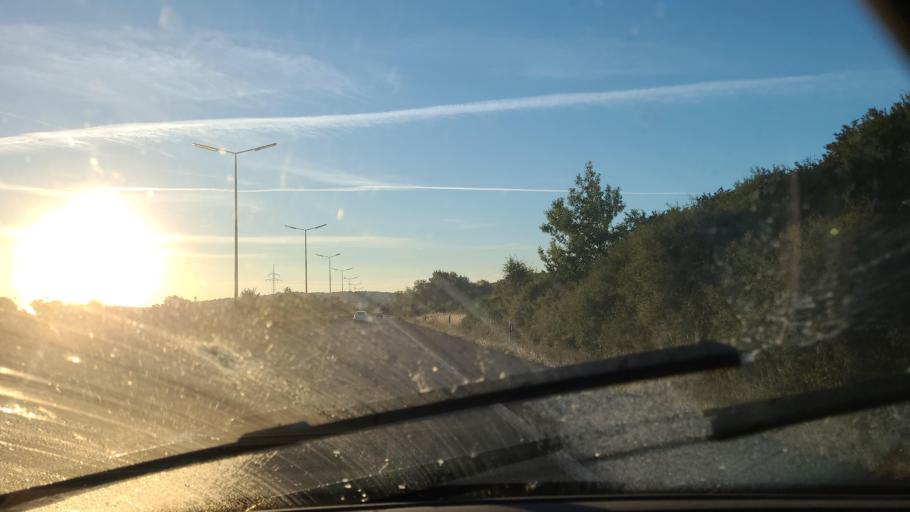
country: LU
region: Luxembourg
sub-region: Canton de Capellen
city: Bascharage
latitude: 49.5495
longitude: 5.9109
